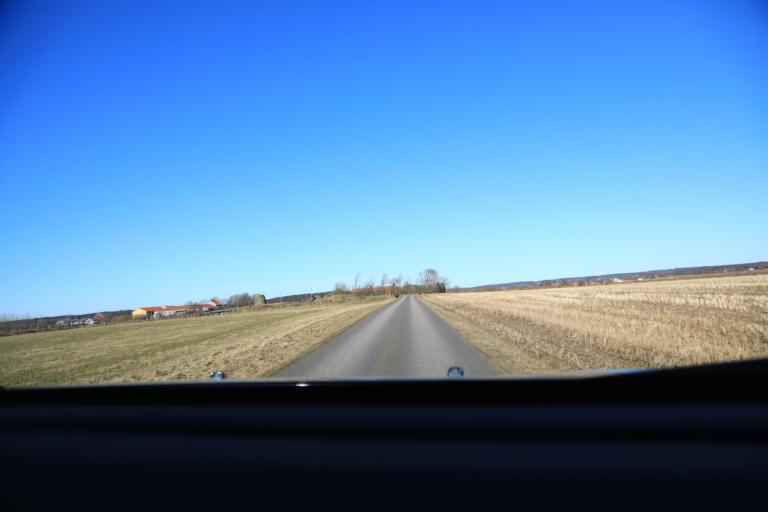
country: SE
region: Halland
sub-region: Kungsbacka Kommun
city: Frillesas
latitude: 57.2291
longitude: 12.1448
